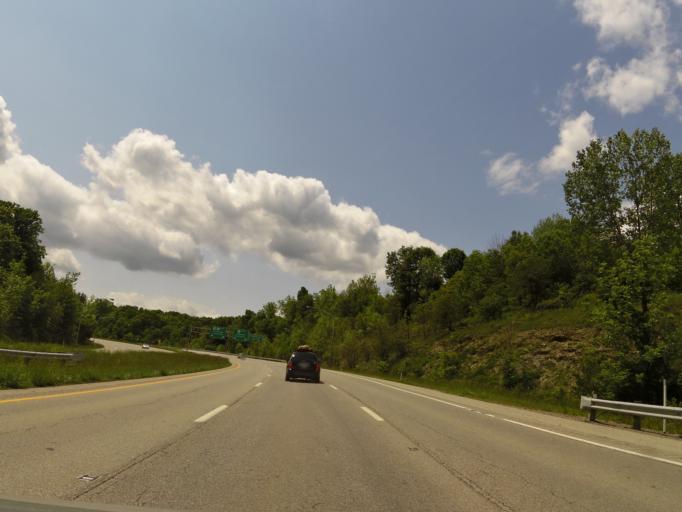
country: US
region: Ohio
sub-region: Athens County
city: Athens
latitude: 39.3113
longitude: -82.1045
